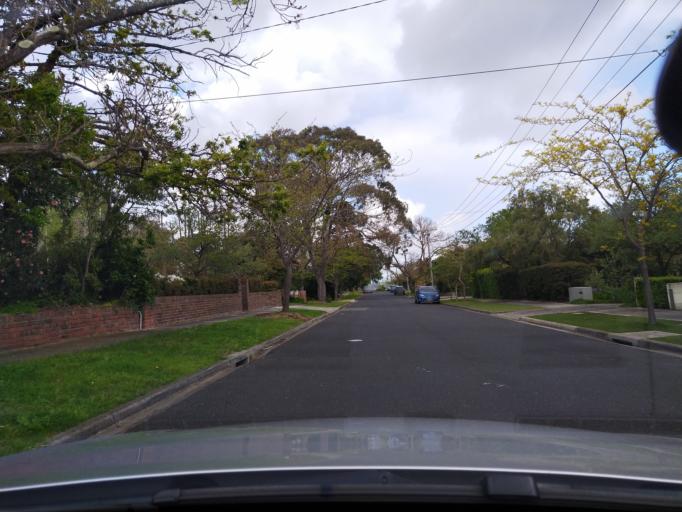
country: AU
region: Victoria
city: Ivanhoe East
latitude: -37.7675
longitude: 145.0596
